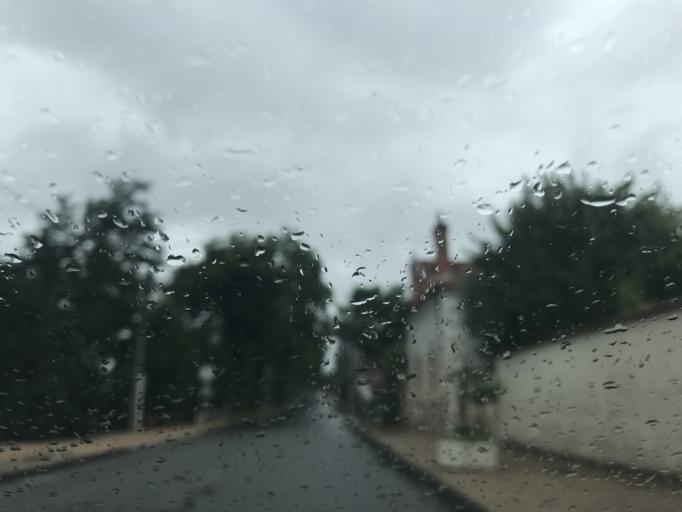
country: FR
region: Auvergne
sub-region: Departement du Puy-de-Dome
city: Ambert
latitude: 45.5554
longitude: 3.7409
